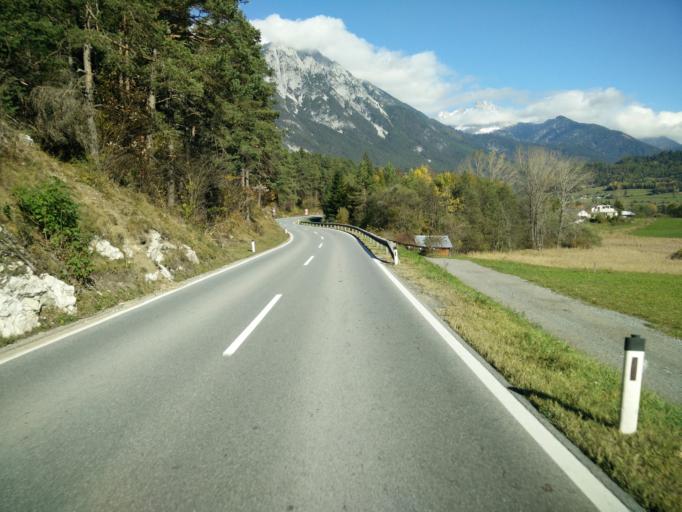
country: AT
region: Tyrol
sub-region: Politischer Bezirk Imst
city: Nassereith
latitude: 47.2966
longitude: 10.8310
